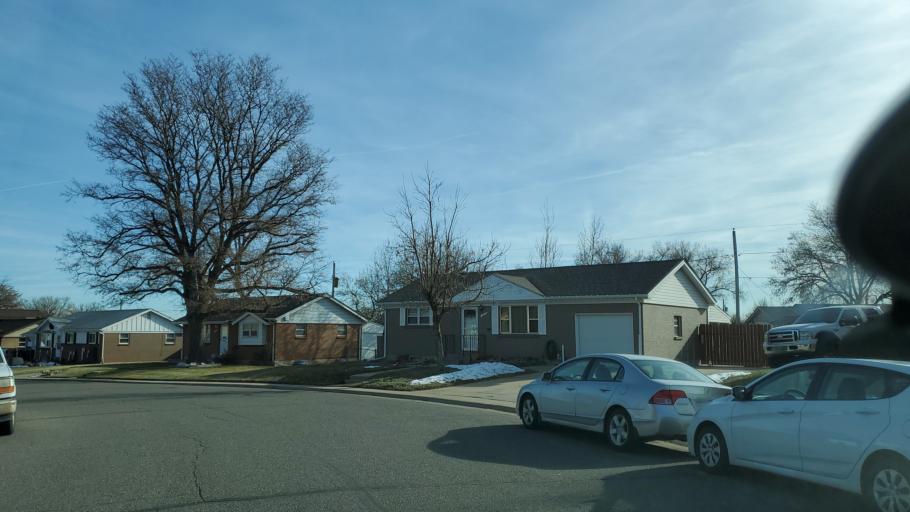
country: US
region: Colorado
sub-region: Adams County
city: Northglenn
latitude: 39.9044
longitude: -104.9639
